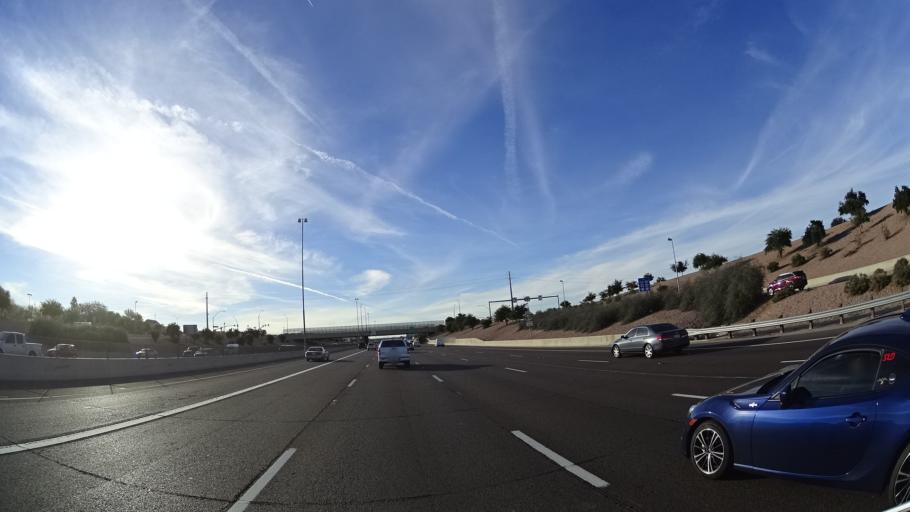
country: US
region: Arizona
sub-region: Maricopa County
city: Gilbert
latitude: 33.3864
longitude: -111.8027
